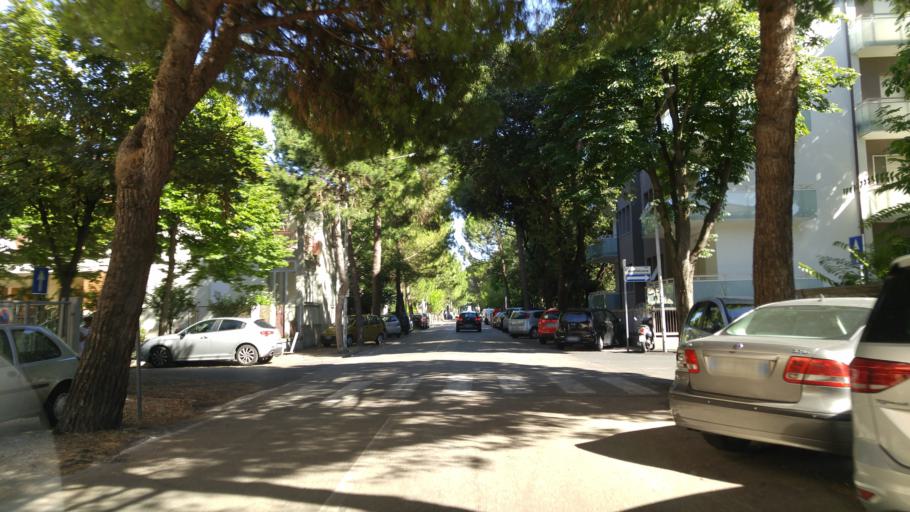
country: IT
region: The Marches
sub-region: Provincia di Pesaro e Urbino
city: Pesaro
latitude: 43.9172
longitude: 12.9085
